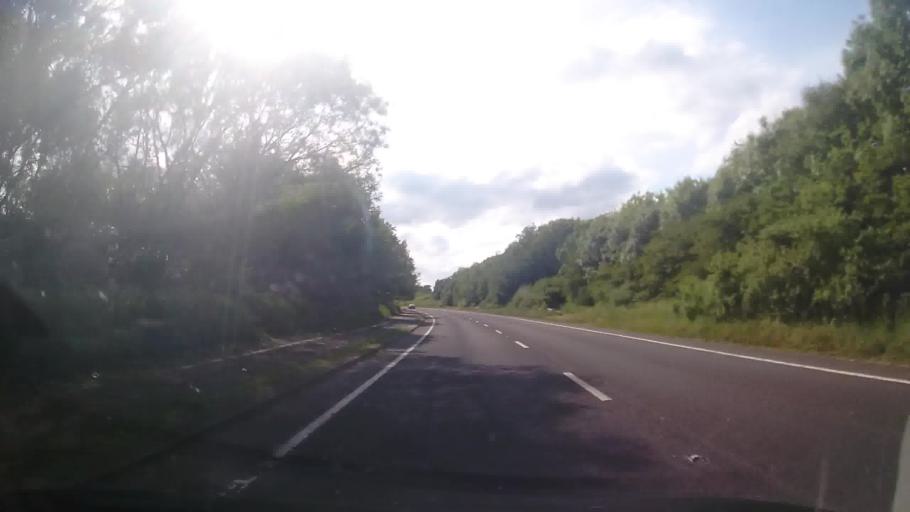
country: GB
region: England
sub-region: Shropshire
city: Astley
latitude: 52.7473
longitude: -2.7353
